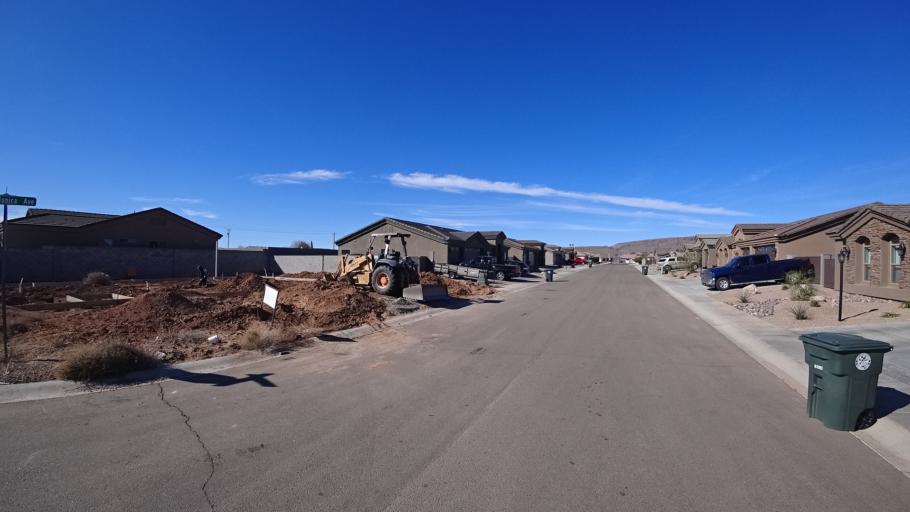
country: US
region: Arizona
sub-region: Mohave County
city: New Kingman-Butler
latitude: 35.2330
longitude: -114.0208
